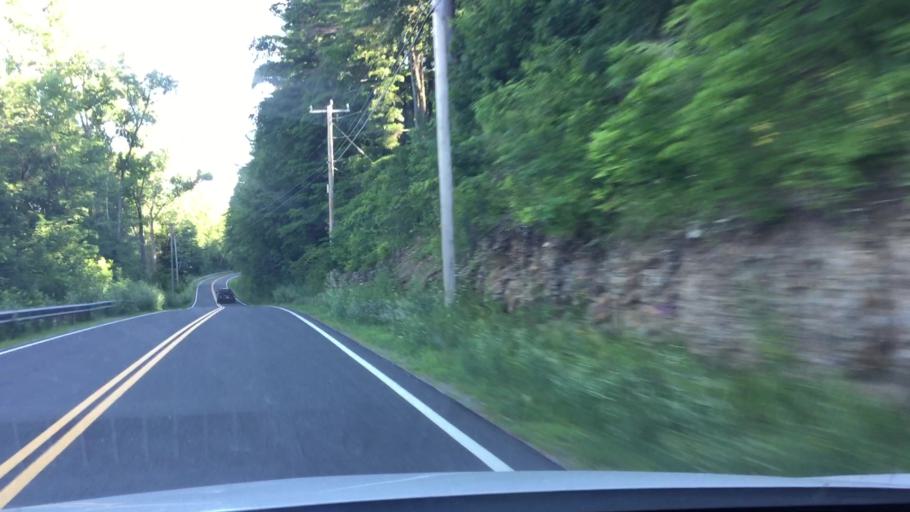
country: US
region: Massachusetts
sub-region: Berkshire County
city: Lee
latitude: 42.2779
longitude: -73.2392
